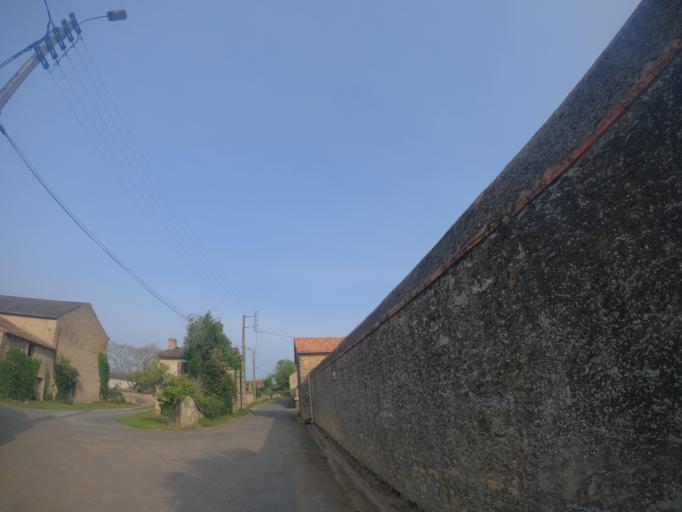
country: FR
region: Poitou-Charentes
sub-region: Departement des Deux-Sevres
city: Saint-Jean-de-Thouars
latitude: 46.9201
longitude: -0.1814
